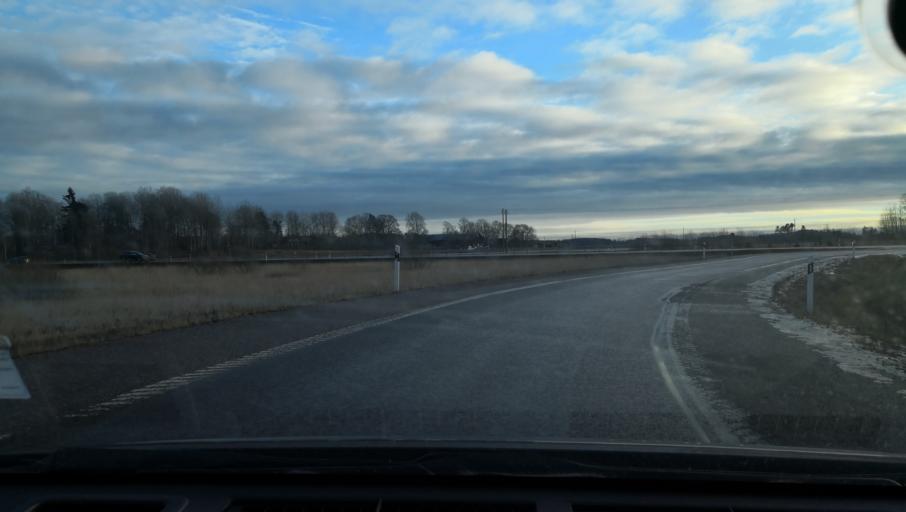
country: SE
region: Vaestmanland
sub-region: Kopings Kommun
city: Koping
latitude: 59.5713
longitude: 16.0912
